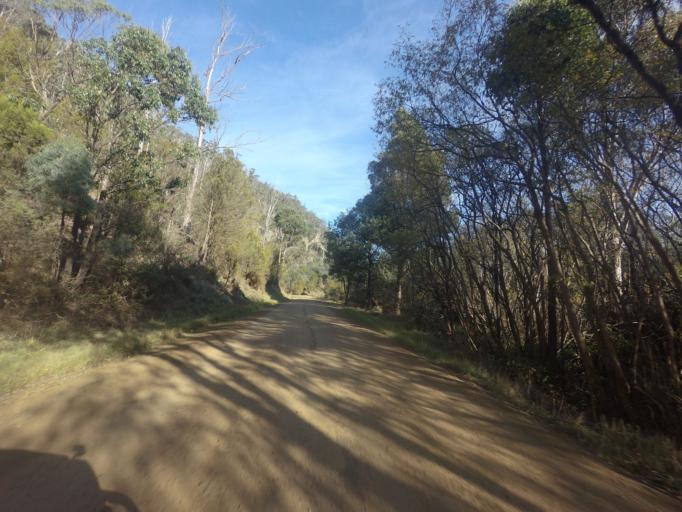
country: AU
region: Tasmania
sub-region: Sorell
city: Sorell
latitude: -42.4944
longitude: 147.4334
